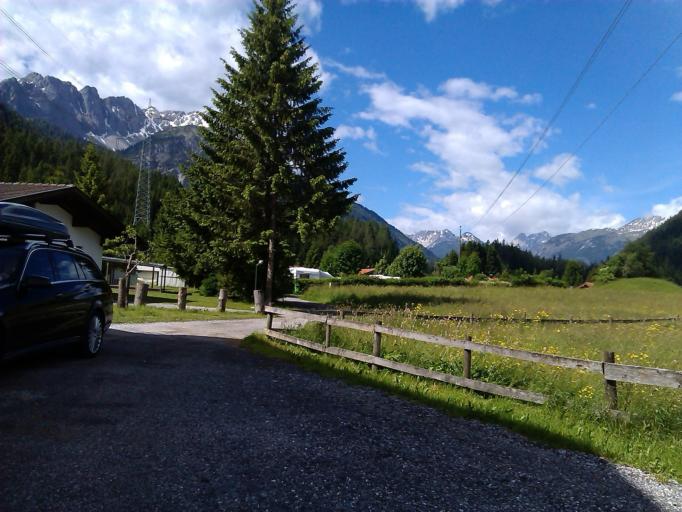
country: AT
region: Tyrol
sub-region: Politischer Bezirk Reutte
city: Biberwier
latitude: 47.3824
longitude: 10.9017
